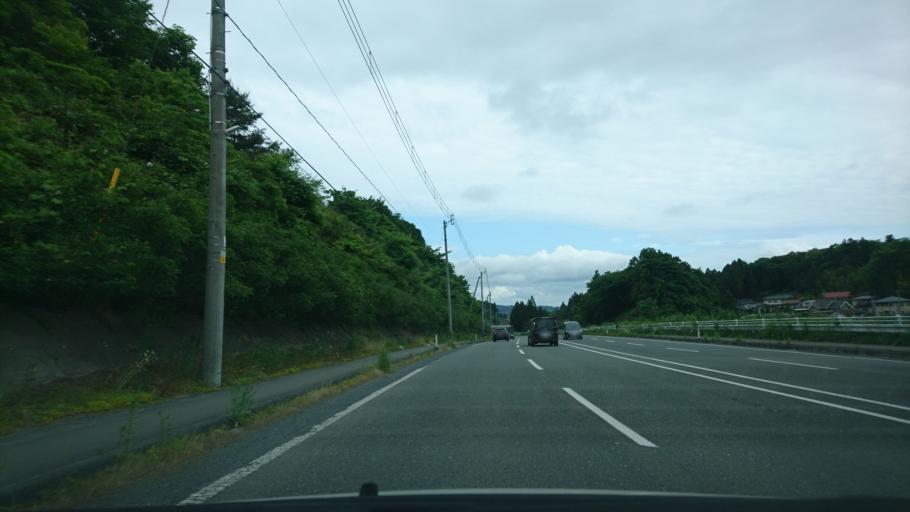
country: JP
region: Iwate
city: Ichinoseki
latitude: 38.9101
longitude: 141.1453
